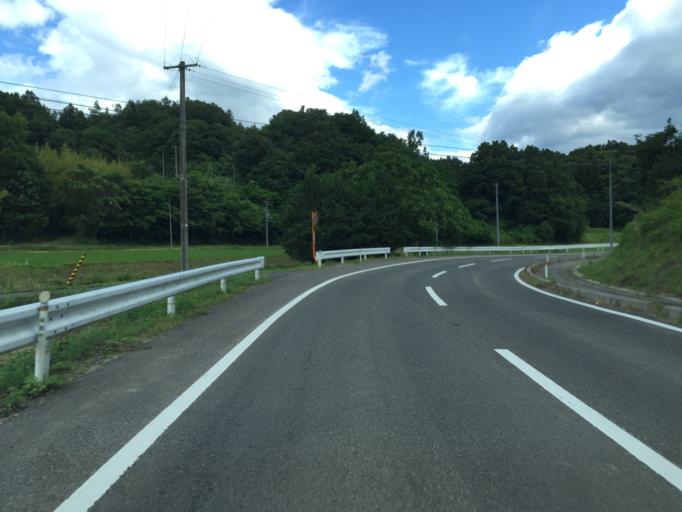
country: JP
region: Fukushima
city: Fukushima-shi
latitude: 37.6837
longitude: 140.5214
